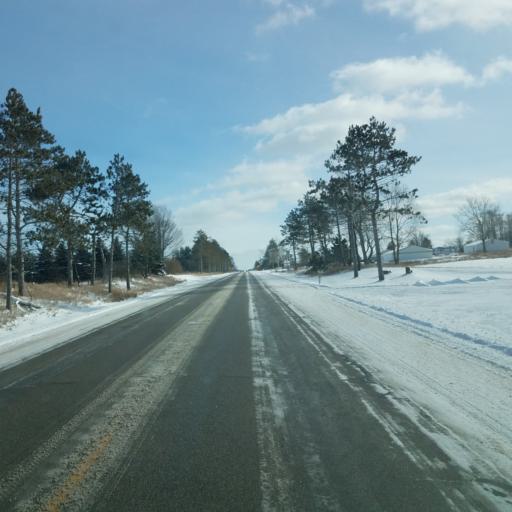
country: US
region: Michigan
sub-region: Osceola County
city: Evart
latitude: 43.9007
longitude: -85.1571
